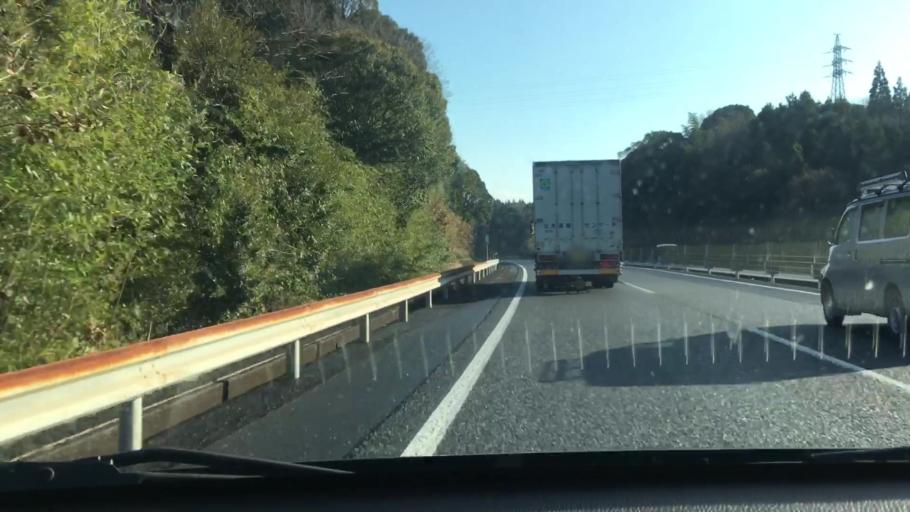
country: JP
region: Kagoshima
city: Okuchi-shinohara
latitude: 31.9158
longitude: 130.7032
